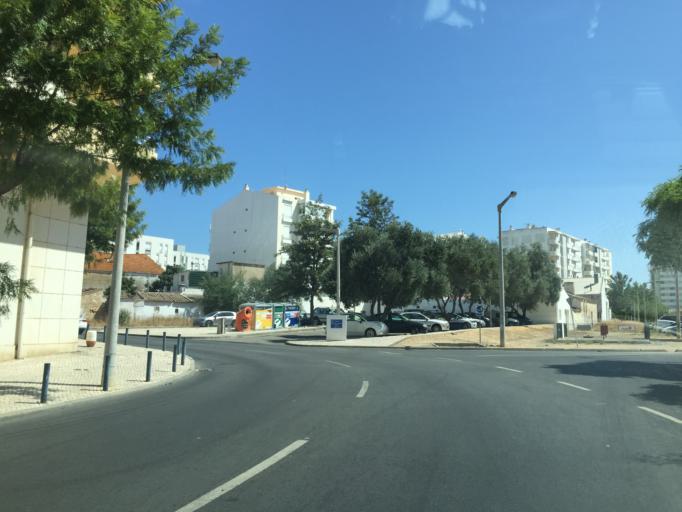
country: PT
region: Faro
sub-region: Faro
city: Faro
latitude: 37.0276
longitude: -7.9409
